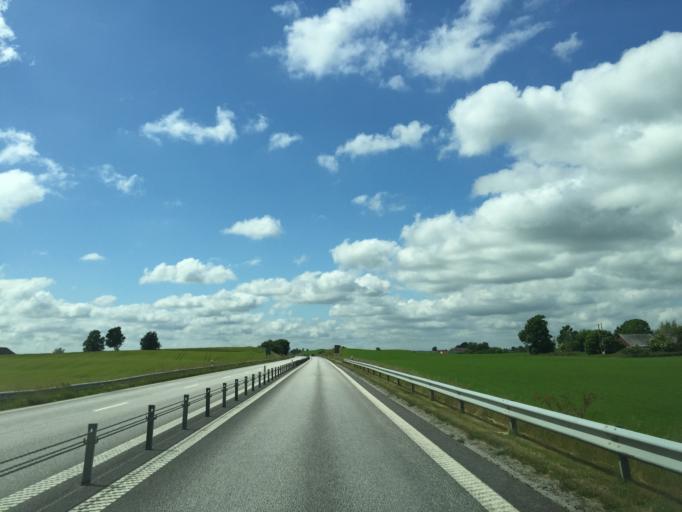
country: SE
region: Skane
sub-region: Skurups Kommun
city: Rydsgard
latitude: 55.4798
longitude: 13.6240
